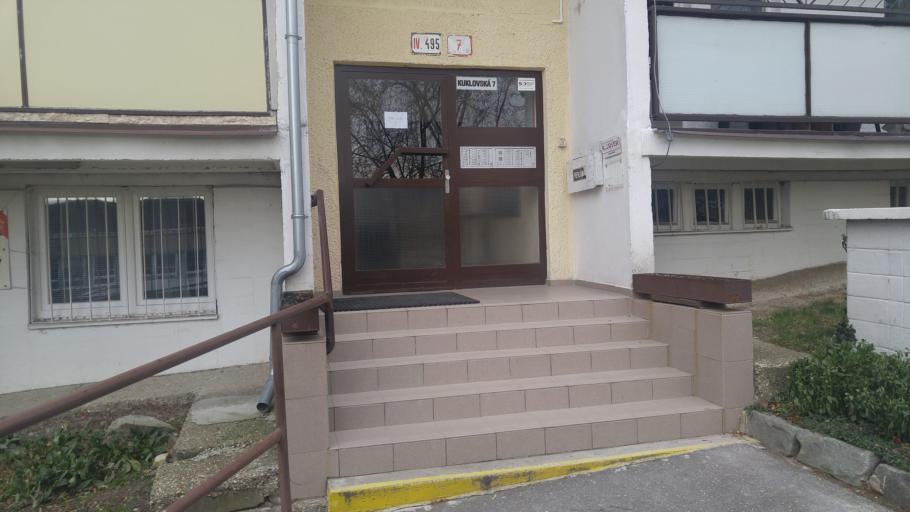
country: AT
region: Lower Austria
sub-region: Politischer Bezirk Bruck an der Leitha
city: Wolfsthal
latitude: 48.1627
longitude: 17.0459
